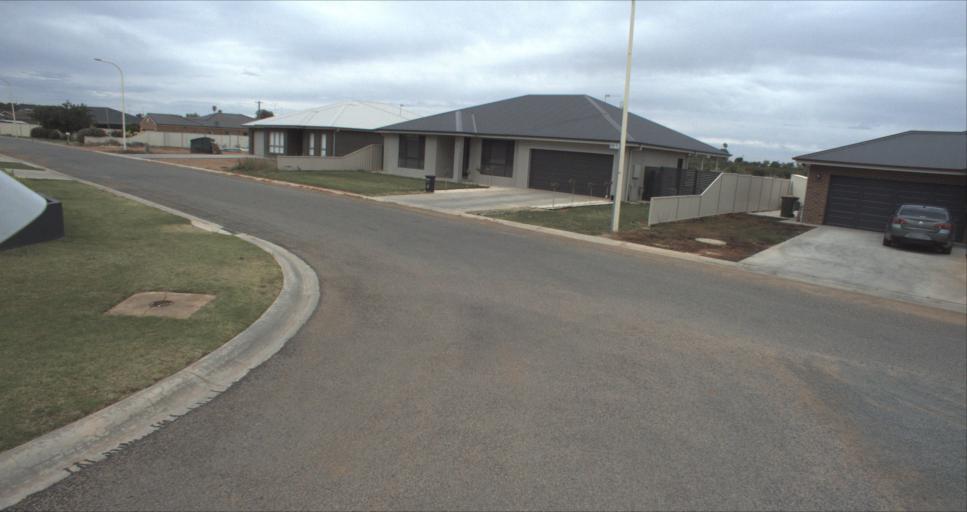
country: AU
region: New South Wales
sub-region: Leeton
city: Leeton
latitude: -34.5403
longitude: 146.3998
